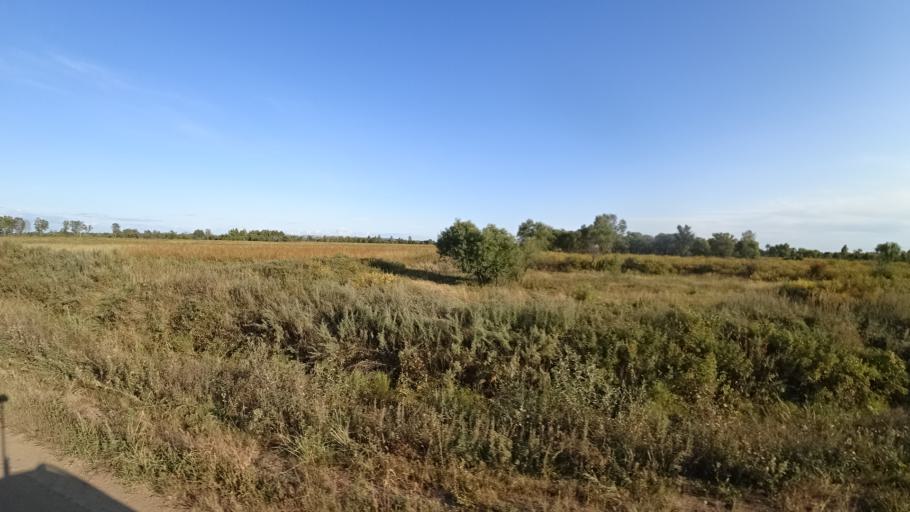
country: RU
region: Amur
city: Arkhara
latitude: 49.3515
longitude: 130.1322
